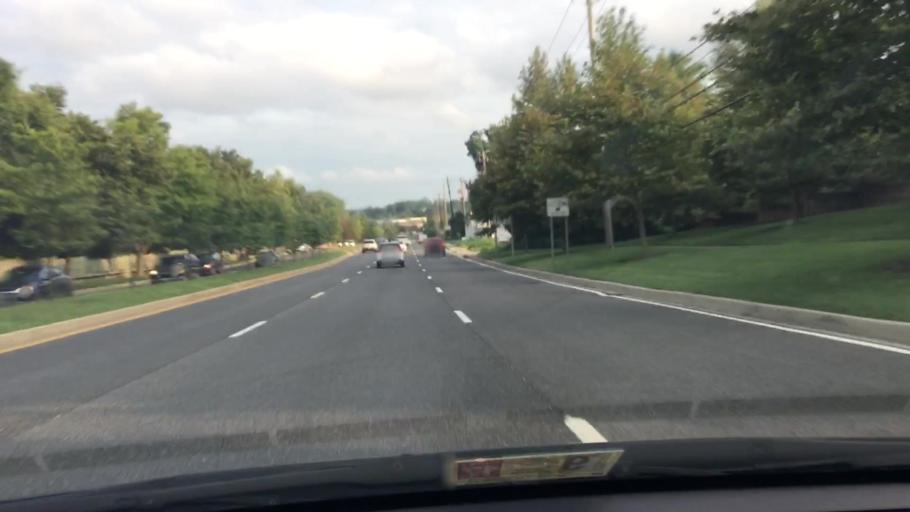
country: US
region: Maryland
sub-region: Montgomery County
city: Germantown
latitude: 39.1891
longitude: -77.2413
